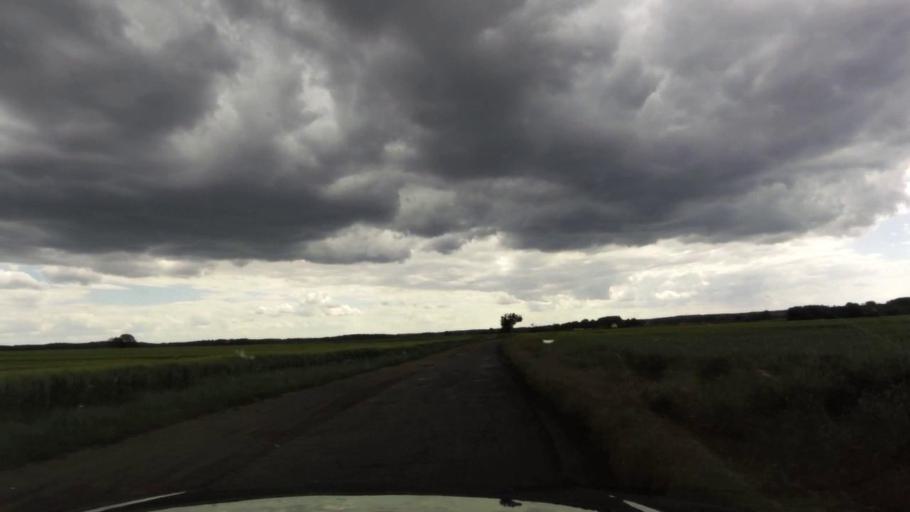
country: PL
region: West Pomeranian Voivodeship
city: Trzcinsko Zdroj
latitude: 52.9491
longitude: 14.6054
